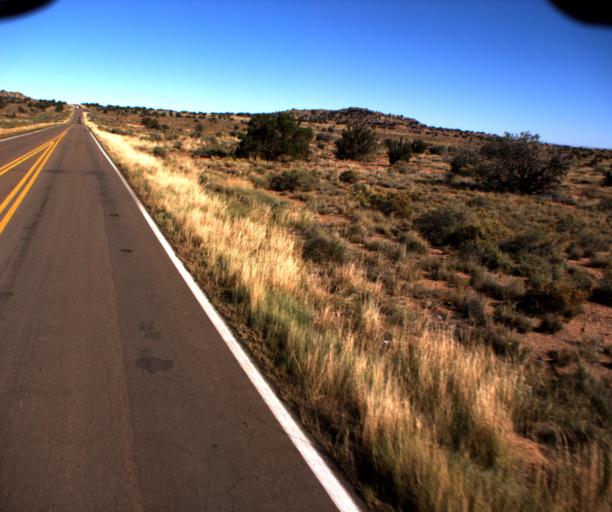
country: US
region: Arizona
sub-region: Navajo County
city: Snowflake
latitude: 34.6789
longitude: -110.1035
